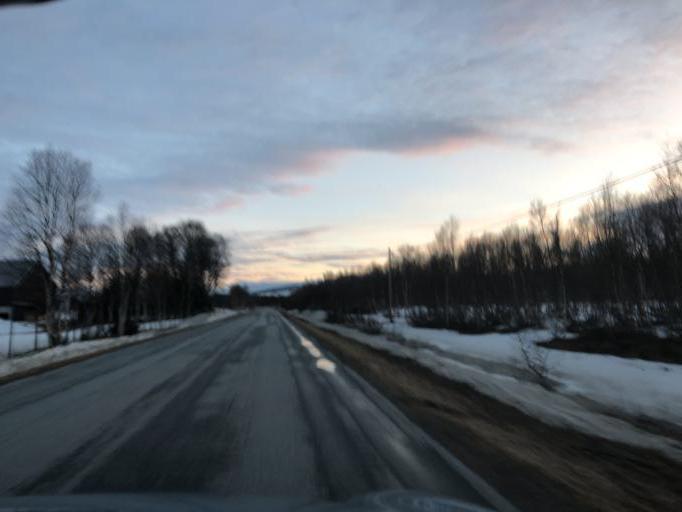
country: NO
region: Sor-Trondelag
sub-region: Tydal
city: Aas
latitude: 62.6750
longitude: 11.8365
